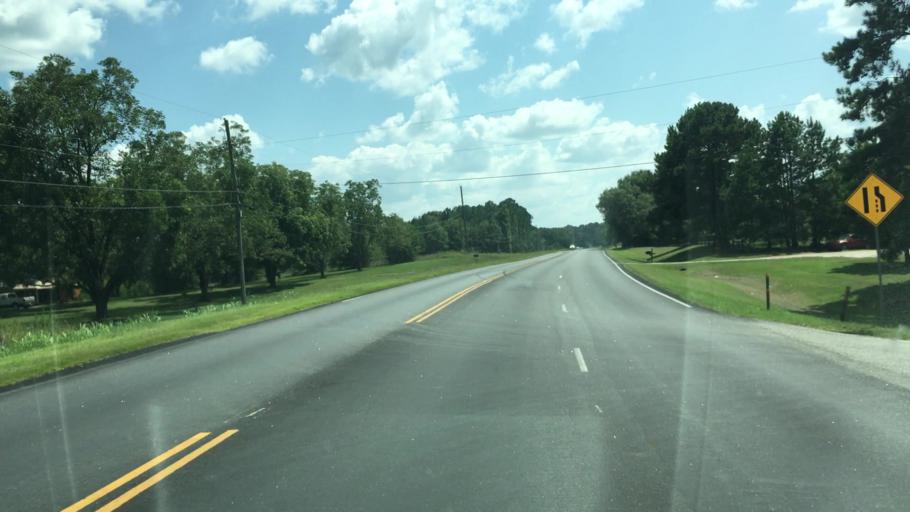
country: US
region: Georgia
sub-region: Morgan County
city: Madison
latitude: 33.6269
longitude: -83.4500
